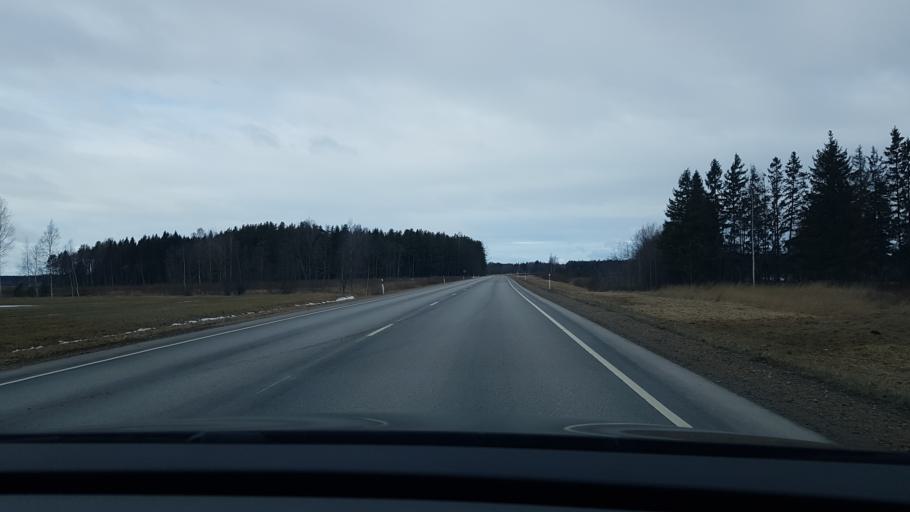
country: EE
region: Paernumaa
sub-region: Paikuse vald
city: Paikuse
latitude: 58.2686
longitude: 24.6416
